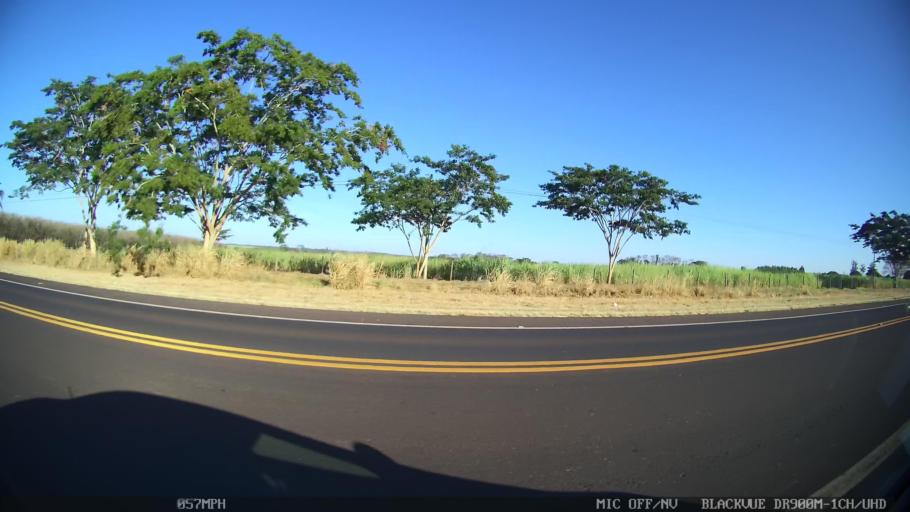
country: BR
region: Sao Paulo
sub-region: Olimpia
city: Olimpia
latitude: -20.7135
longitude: -48.9868
